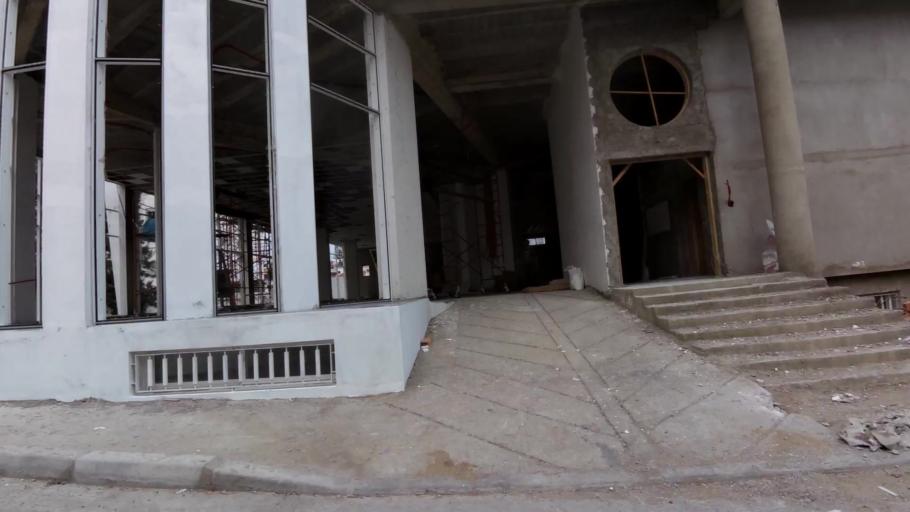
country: MA
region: Tanger-Tetouan
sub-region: Tanger-Assilah
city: Tangier
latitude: 35.7648
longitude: -5.7994
